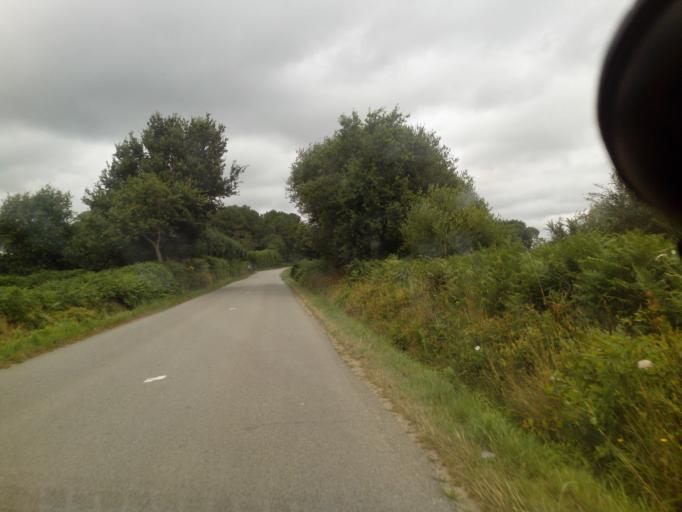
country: FR
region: Brittany
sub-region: Departement du Morbihan
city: Kervignac
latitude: 47.7534
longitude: -3.2705
